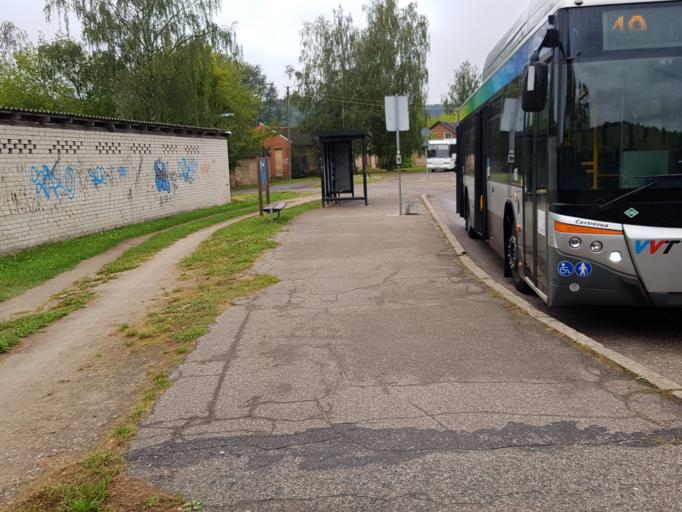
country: LT
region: Vilnius County
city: Lazdynai
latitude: 54.6550
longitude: 25.1960
